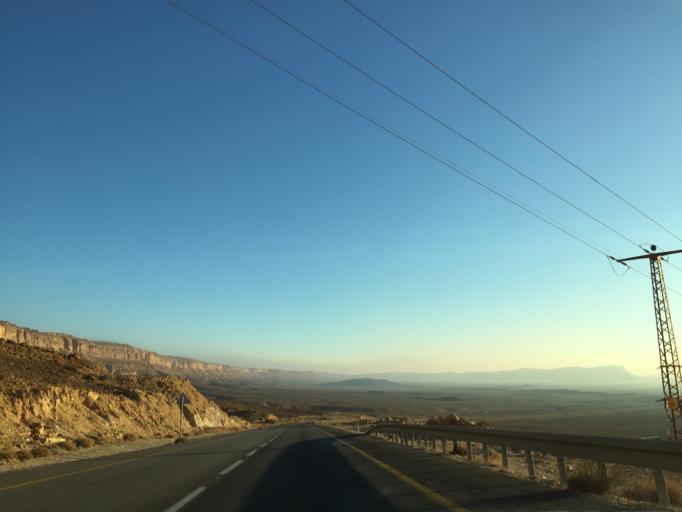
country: IL
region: Southern District
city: Mitzpe Ramon
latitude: 30.6226
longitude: 34.8206
